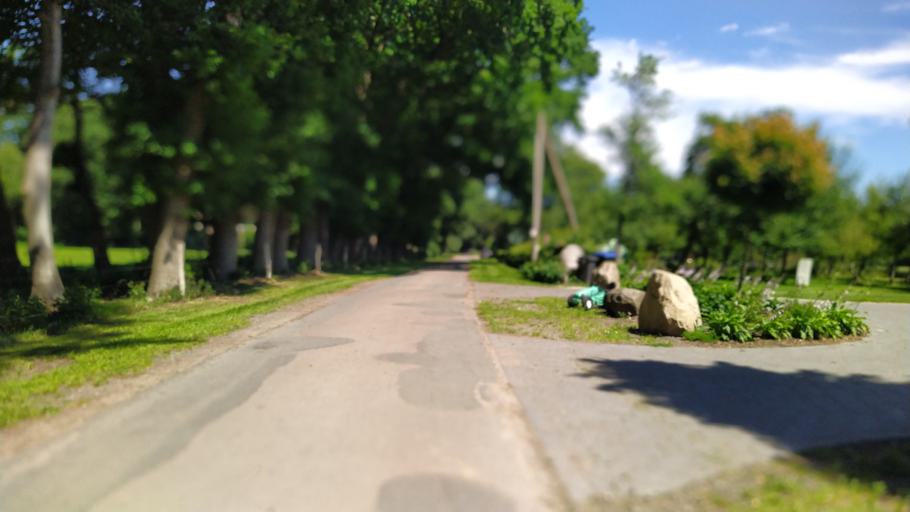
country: DE
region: Lower Saxony
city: Bargstedt
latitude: 53.4941
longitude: 9.4358
